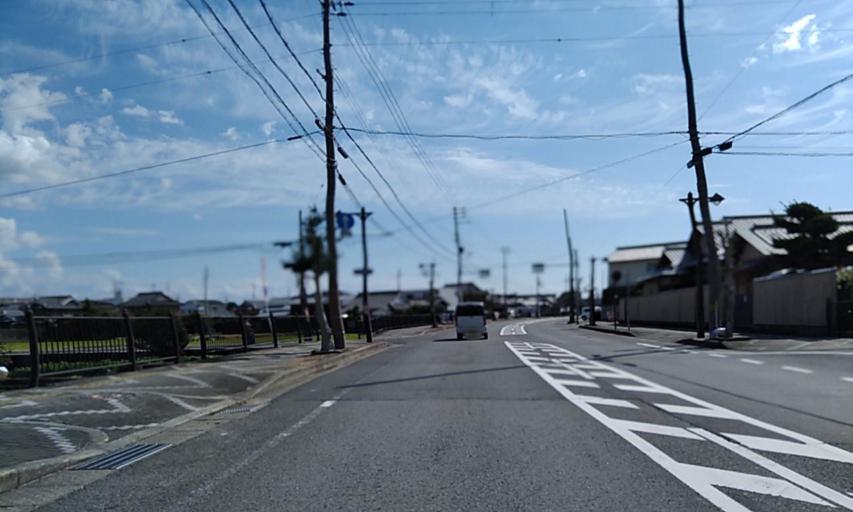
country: JP
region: Wakayama
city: Gobo
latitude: 33.9055
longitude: 135.1606
